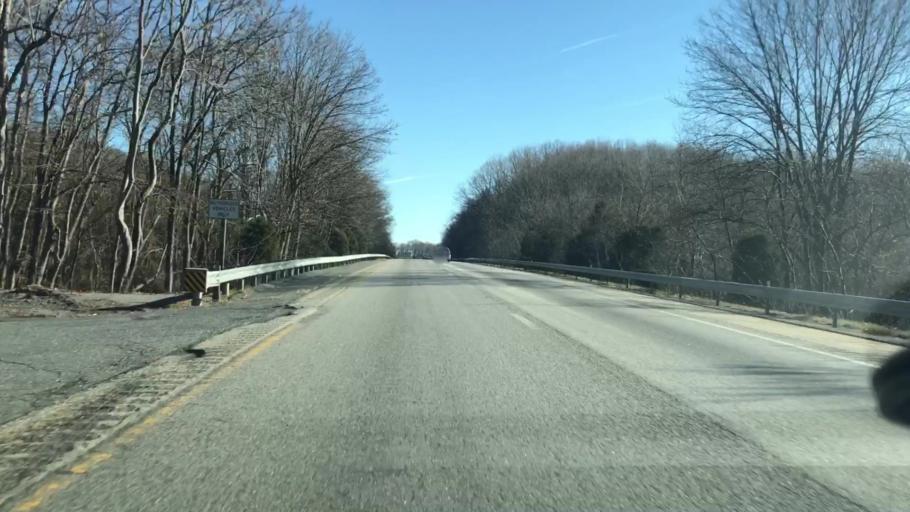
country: US
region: Virginia
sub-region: Botetourt County
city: Buchanan
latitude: 37.6109
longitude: -79.6038
